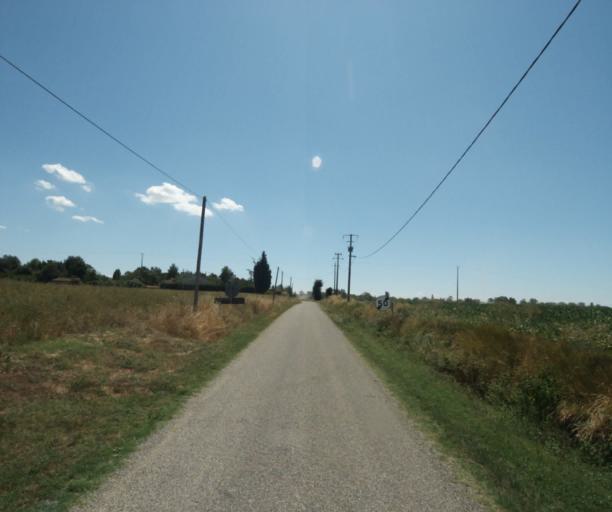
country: FR
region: Midi-Pyrenees
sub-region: Departement de la Haute-Garonne
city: Saint-Felix-Lauragais
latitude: 43.4549
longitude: 1.9462
